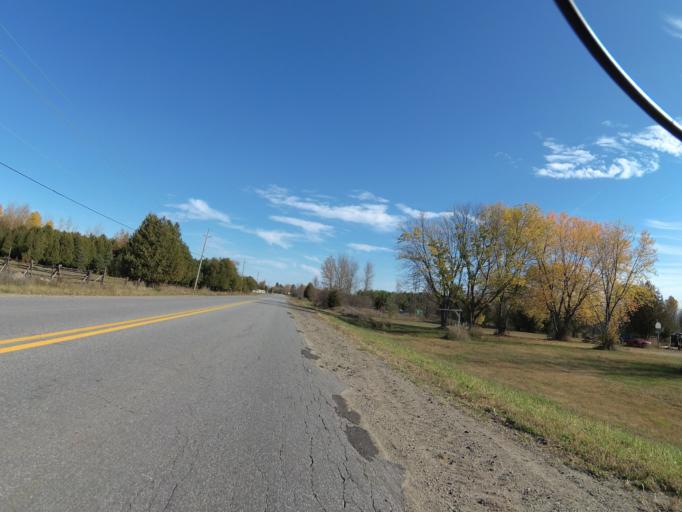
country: CA
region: Ontario
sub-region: Lanark County
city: Smiths Falls
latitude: 44.8368
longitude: -75.9399
